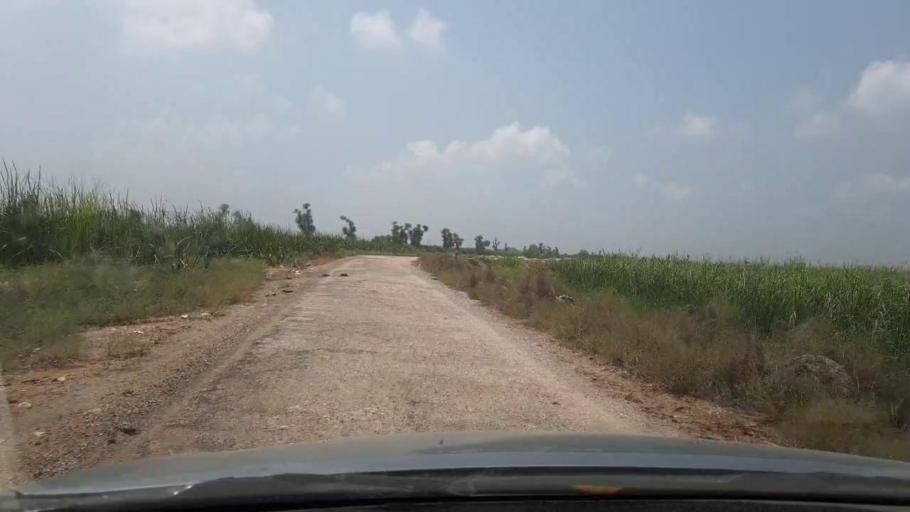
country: PK
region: Sindh
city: Khairpur
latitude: 27.4814
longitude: 68.7069
